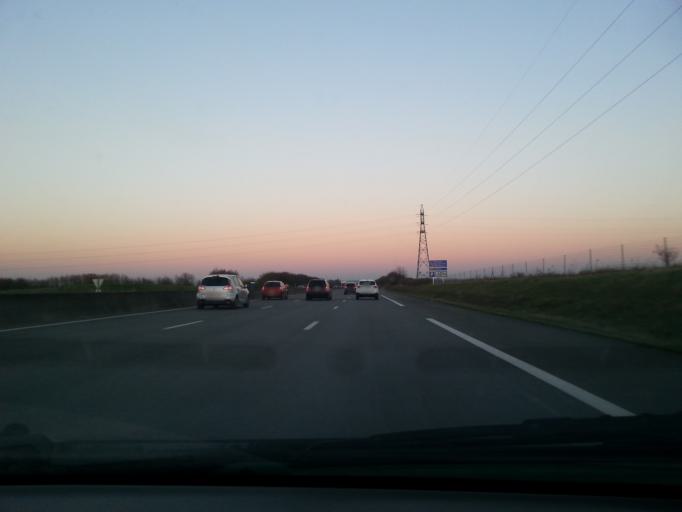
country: FR
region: Centre
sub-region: Departement d'Eure-et-Loir
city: Dammarie
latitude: 48.3699
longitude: 1.4611
